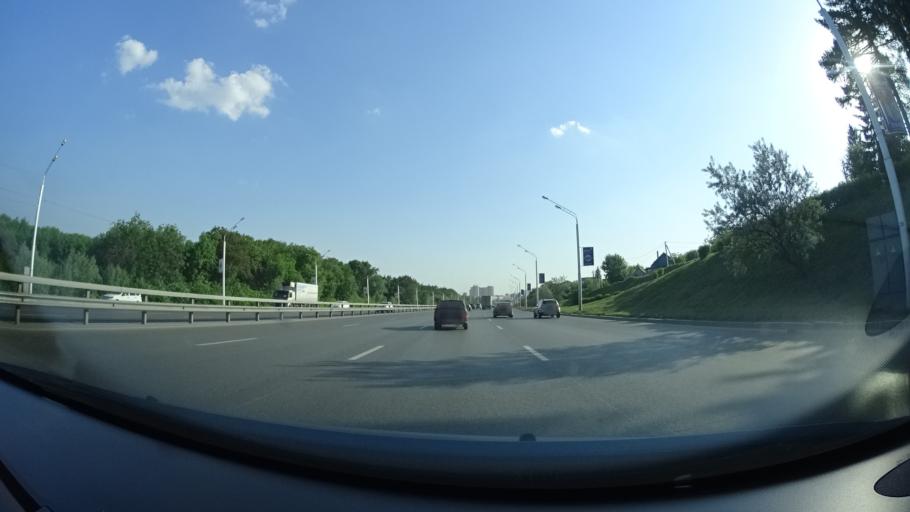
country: RU
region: Bashkortostan
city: Ufa
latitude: 54.7362
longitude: 56.0054
